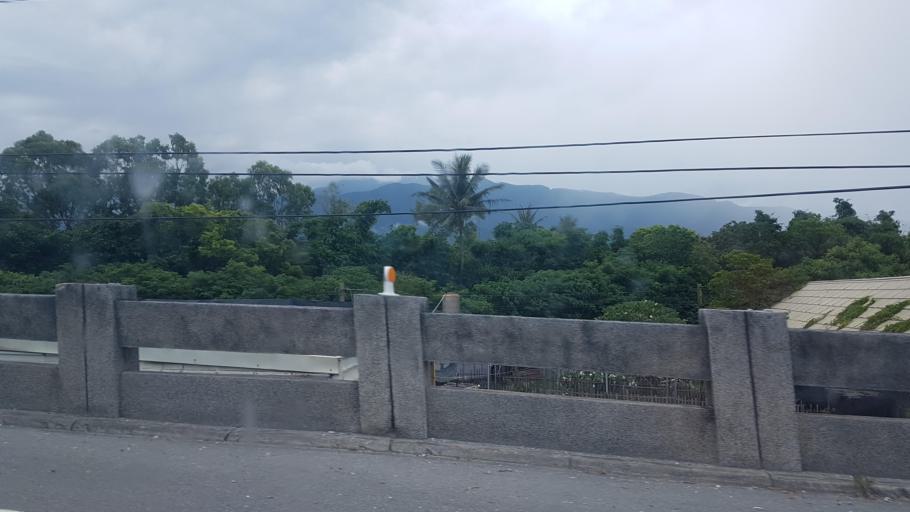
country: TW
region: Taiwan
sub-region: Hualien
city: Hualian
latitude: 24.0042
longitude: 121.6348
